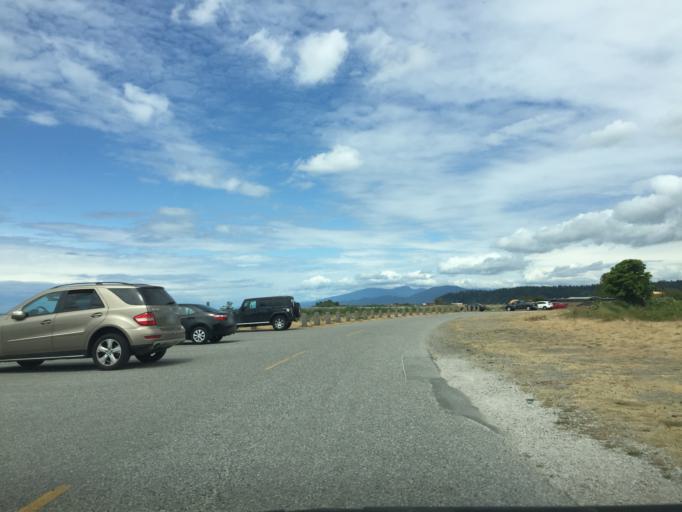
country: CA
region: British Columbia
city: Richmond
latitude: 49.2174
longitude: -123.2126
